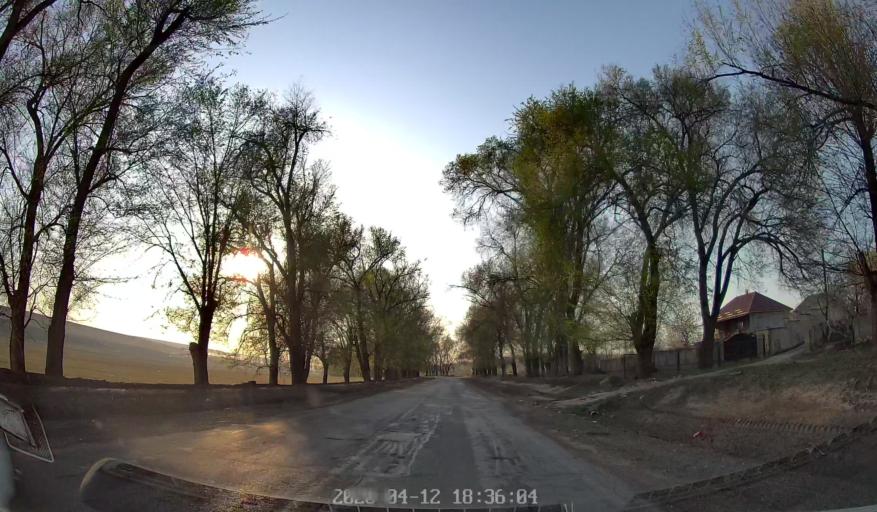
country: MD
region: Chisinau
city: Vadul lui Voda
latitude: 47.1158
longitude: 29.0363
